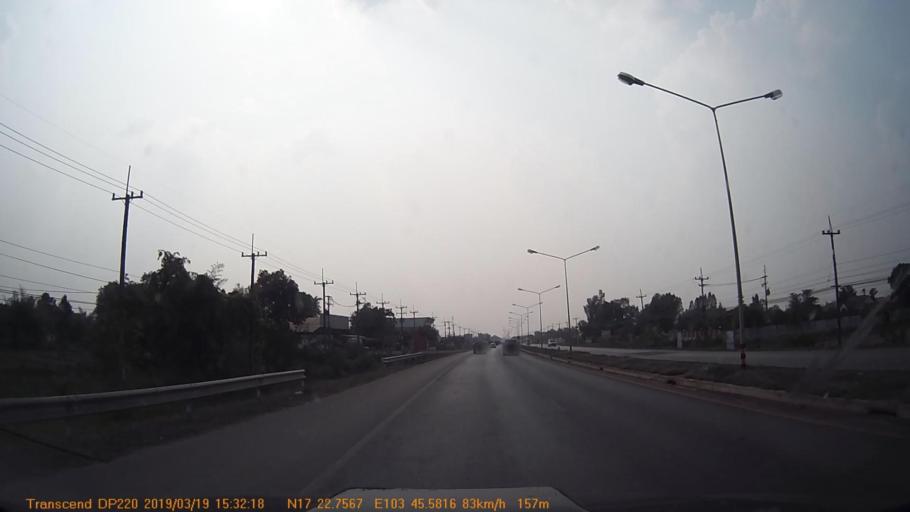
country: TH
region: Sakon Nakhon
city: Phang Khon
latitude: 17.3793
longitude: 103.7593
